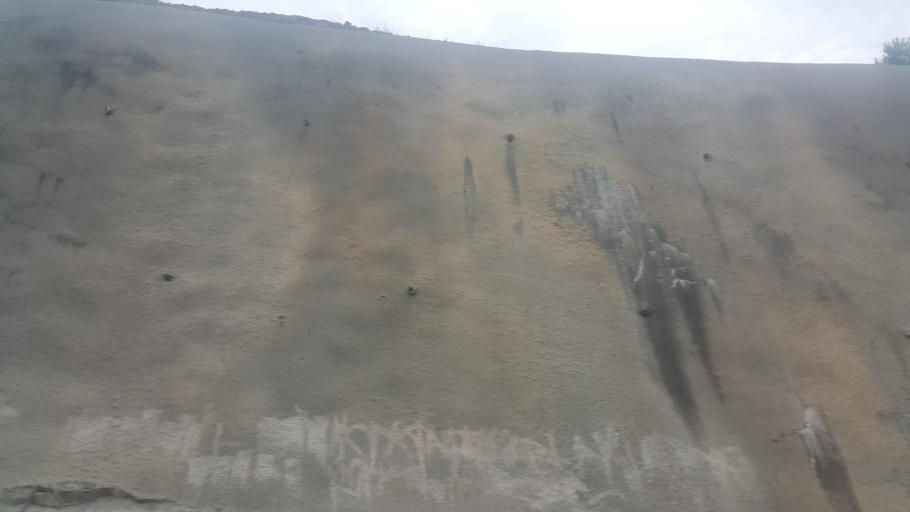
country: TR
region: Nigde
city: Ciftehan
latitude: 37.5201
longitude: 34.8177
